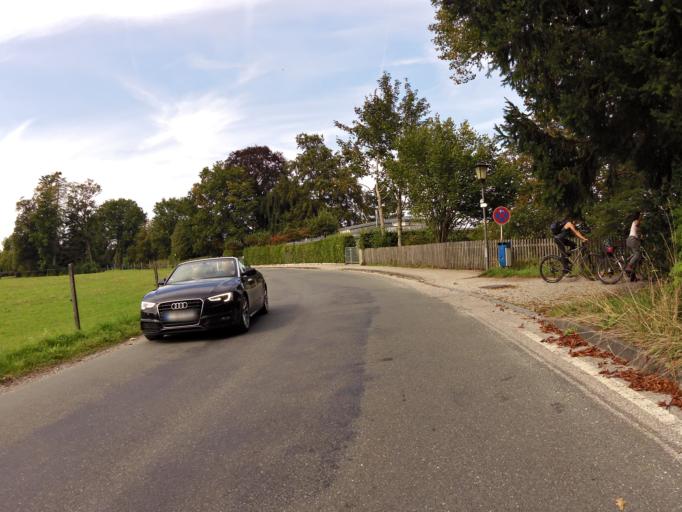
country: DE
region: Bavaria
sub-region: Upper Bavaria
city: Seeshaupt
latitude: 47.8282
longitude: 11.2954
